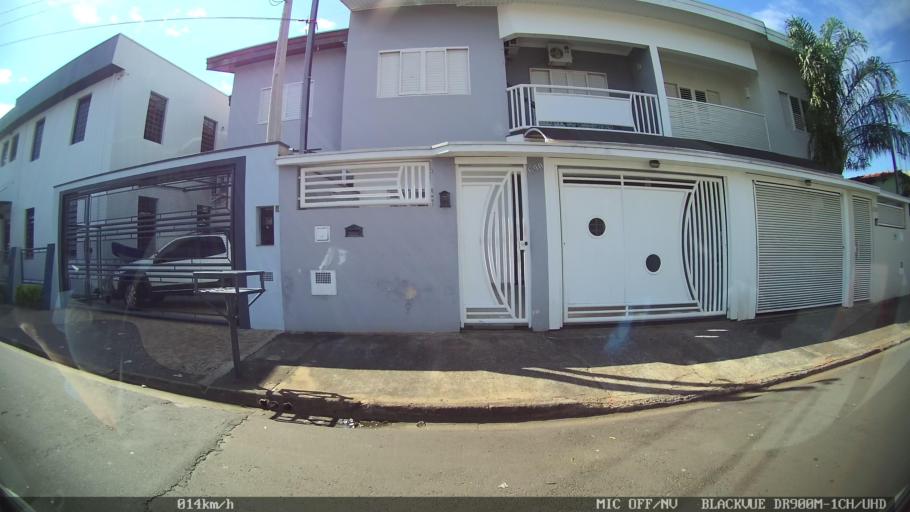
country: BR
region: Sao Paulo
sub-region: Americana
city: Americana
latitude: -22.7420
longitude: -47.3725
